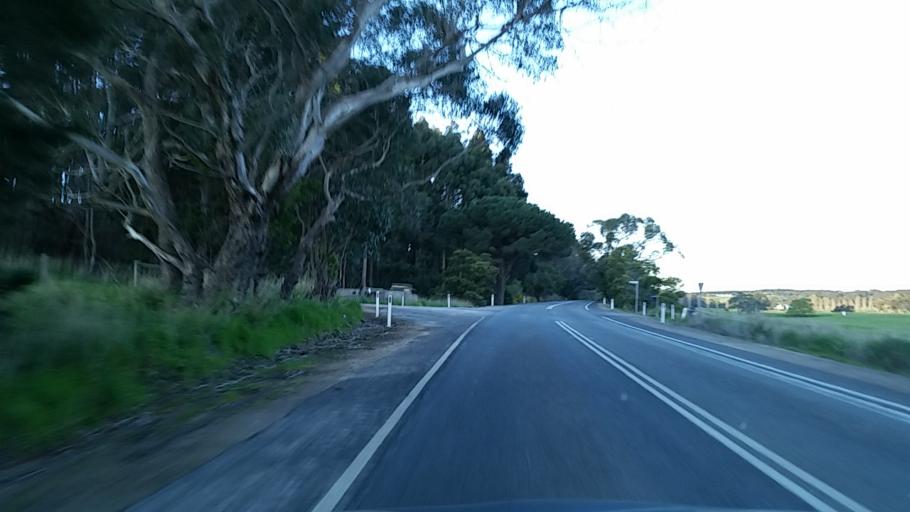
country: AU
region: South Australia
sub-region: Alexandrina
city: Mount Compass
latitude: -35.3159
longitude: 138.5683
